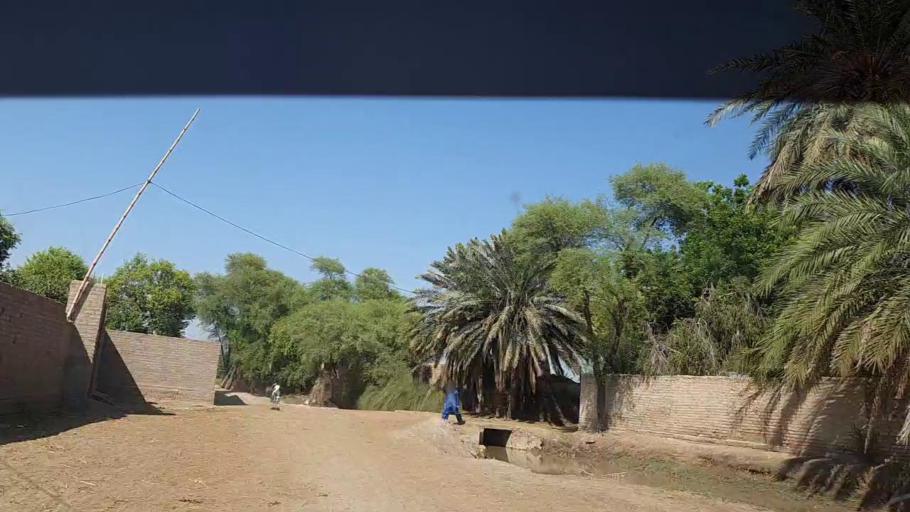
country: PK
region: Sindh
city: Ghauspur
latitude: 28.2042
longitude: 69.0462
